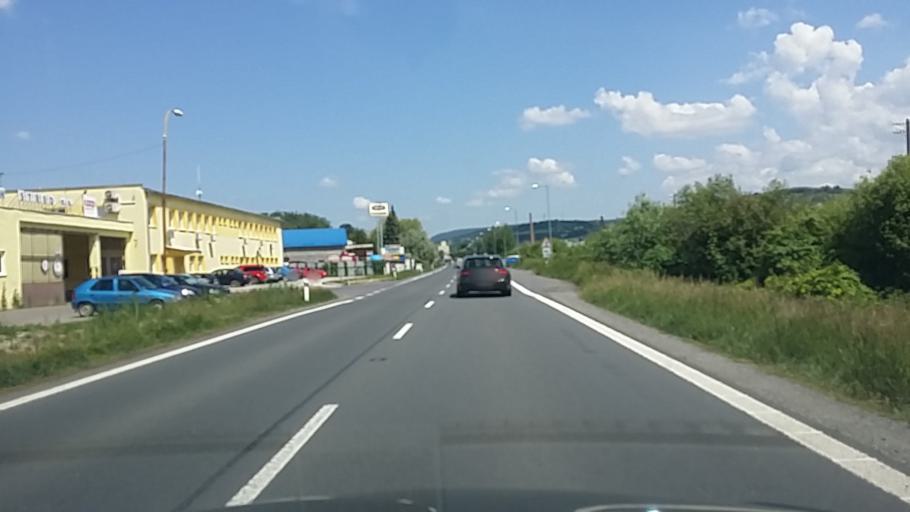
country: SK
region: Banskobystricky
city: Krupina
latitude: 48.3365
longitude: 19.0638
